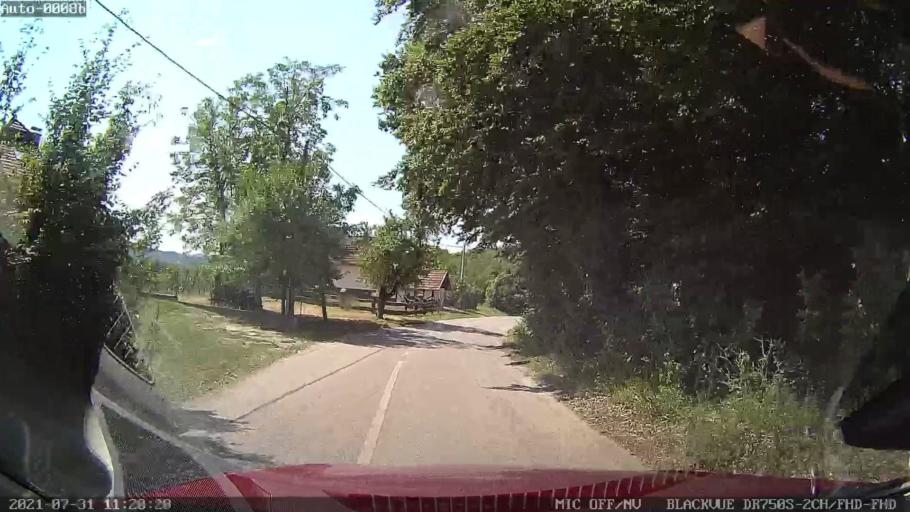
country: HR
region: Varazdinska
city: Jalzabet
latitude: 46.2335
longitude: 16.4747
